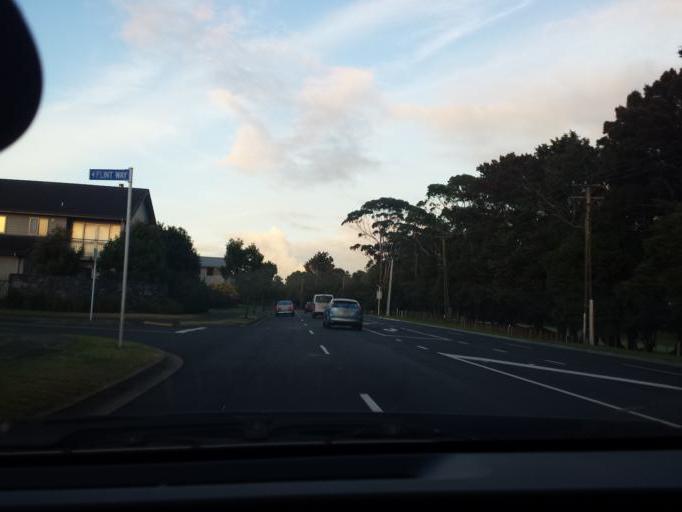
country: NZ
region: Auckland
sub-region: Auckland
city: Tamaki
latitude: -36.8840
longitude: 174.8366
